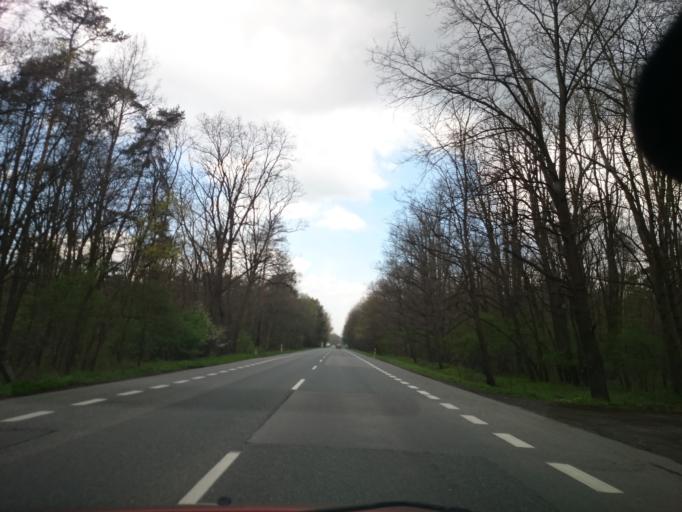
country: PL
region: Opole Voivodeship
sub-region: Powiat opolski
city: Chrzastowice
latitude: 50.6374
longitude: 18.0056
